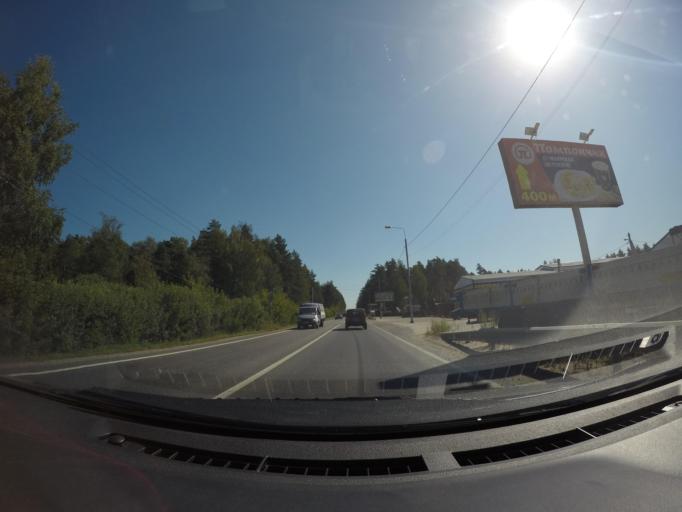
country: RU
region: Moskovskaya
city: Gzhel'
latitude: 55.6338
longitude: 38.3414
